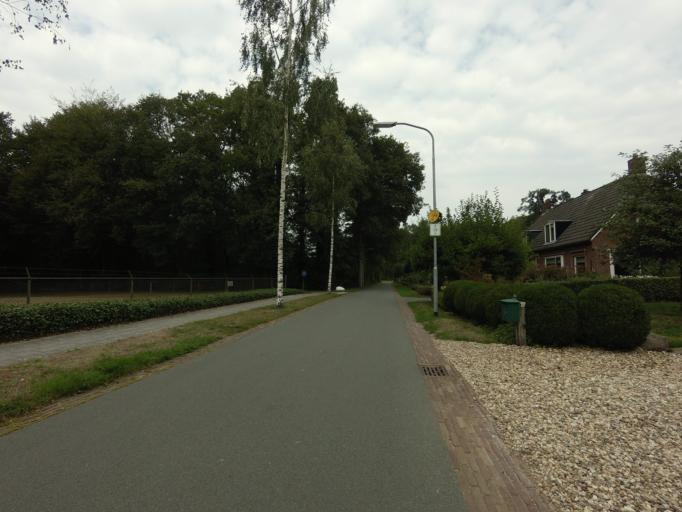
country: NL
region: Drenthe
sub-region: Gemeente Assen
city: Assen
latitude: 52.9874
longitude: 6.6417
